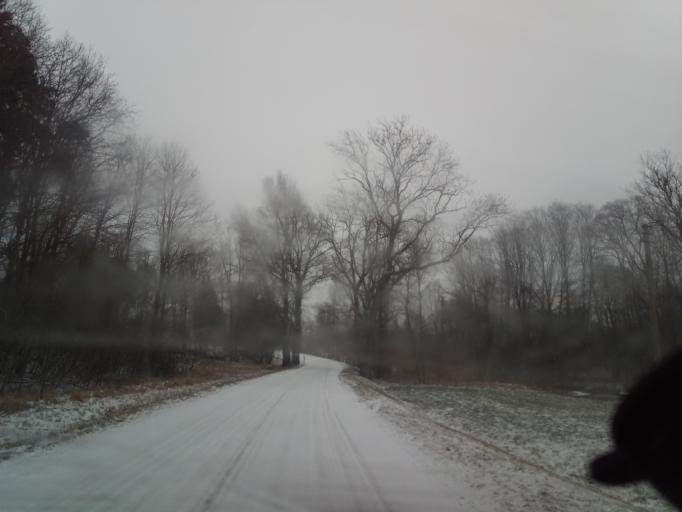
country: LT
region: Utenos apskritis
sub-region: Anyksciai
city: Anyksciai
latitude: 55.4227
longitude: 25.1107
